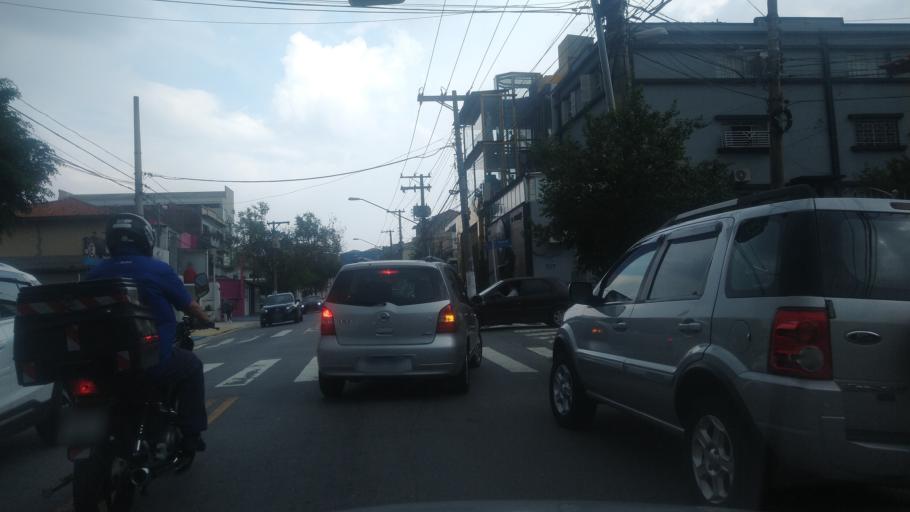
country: BR
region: Sao Paulo
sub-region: Sao Paulo
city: Sao Paulo
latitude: -23.4941
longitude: -46.6167
